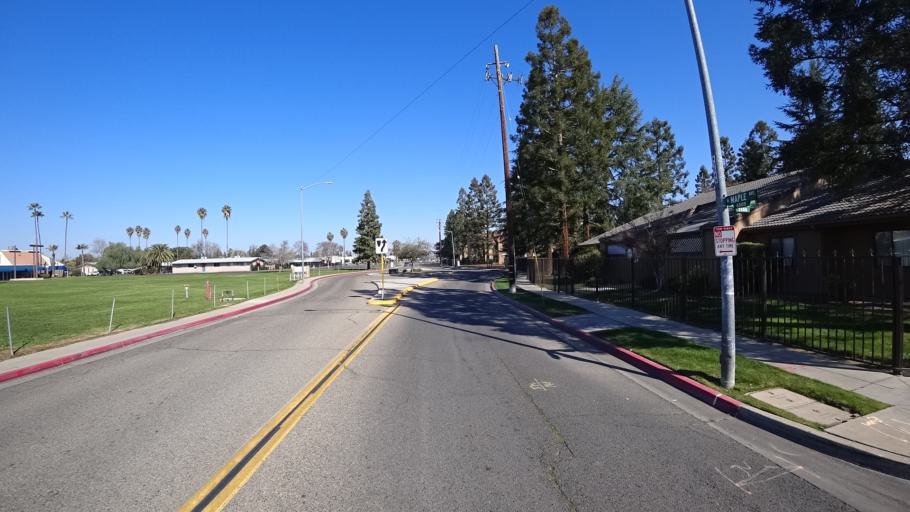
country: US
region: California
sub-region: Fresno County
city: Clovis
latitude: 36.8354
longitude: -119.7452
